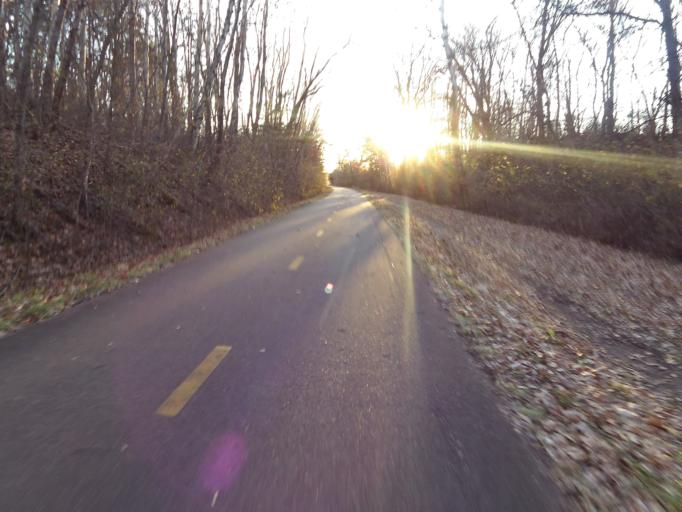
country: US
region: Minnesota
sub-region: Washington County
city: Grant
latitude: 45.1125
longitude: -92.8552
